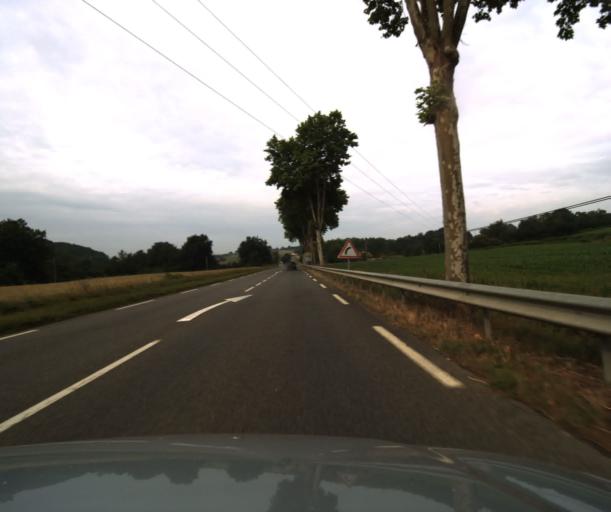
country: FR
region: Midi-Pyrenees
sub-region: Departement du Gers
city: Mirande
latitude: 43.4881
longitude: 0.3563
